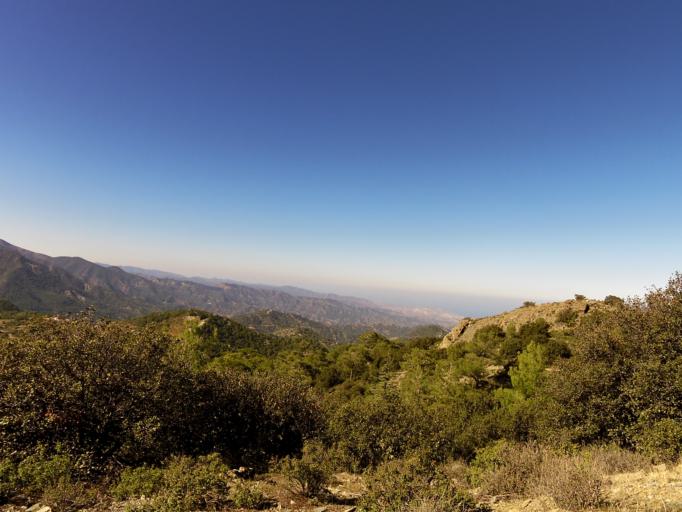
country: CY
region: Limassol
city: Kyperounta
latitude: 34.9535
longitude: 32.9714
